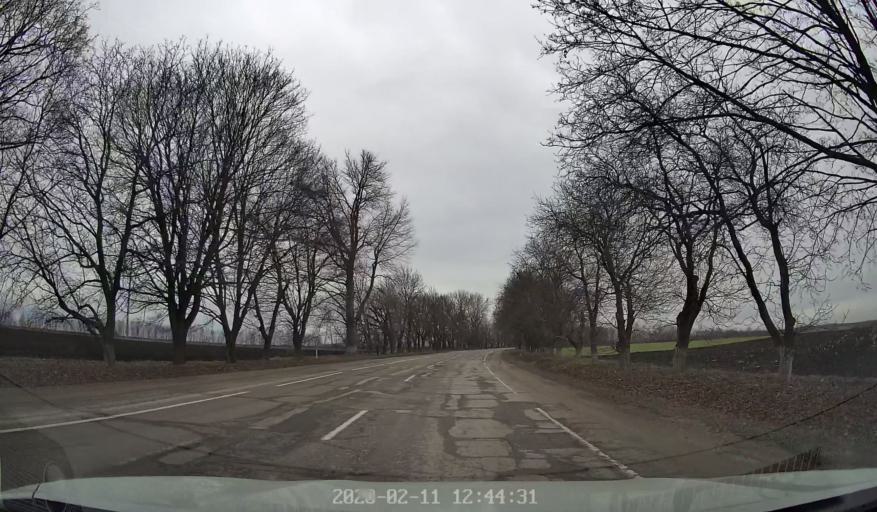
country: MD
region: Raionul Edinet
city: Edinet
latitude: 48.2462
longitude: 27.2008
